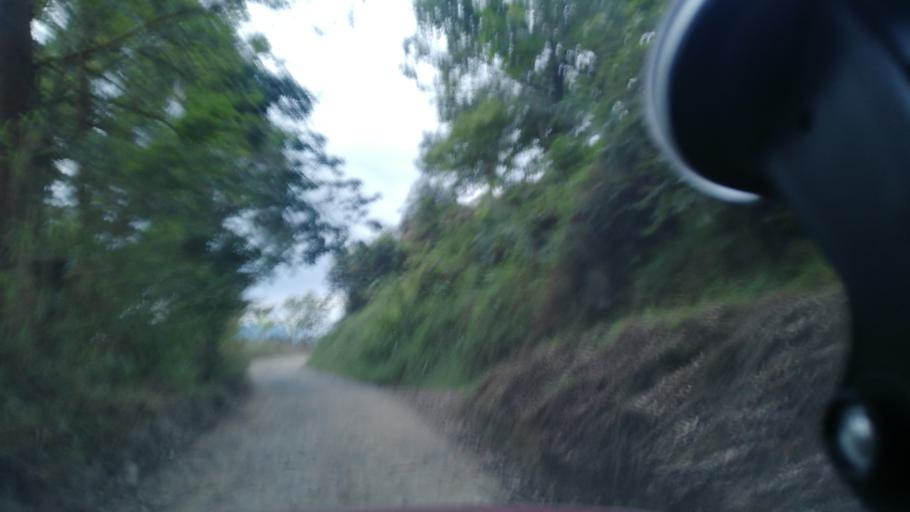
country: CO
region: Cundinamarca
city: Pacho
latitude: 5.1629
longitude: -74.2288
